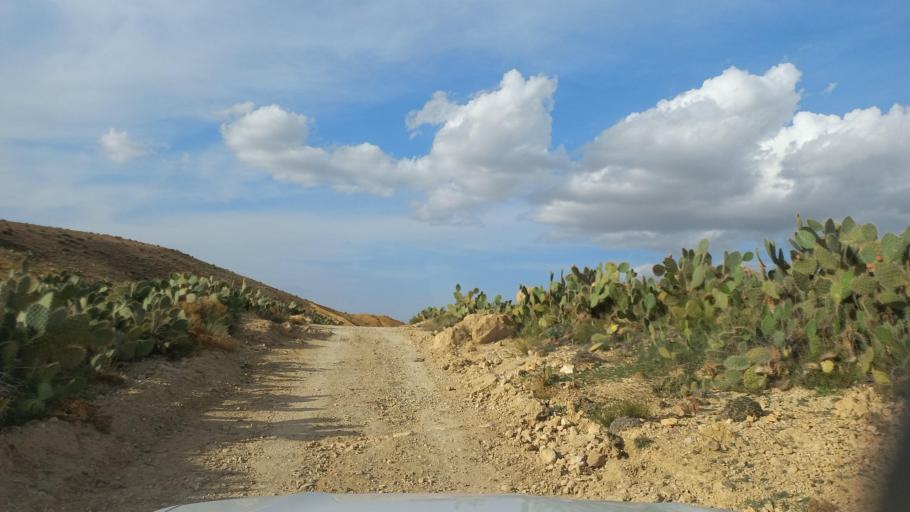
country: TN
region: Al Qasrayn
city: Sbiba
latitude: 35.4585
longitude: 9.0825
